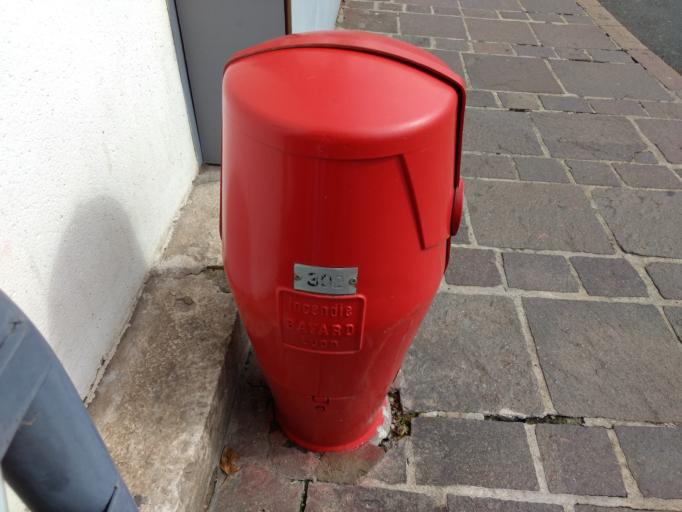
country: FR
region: Midi-Pyrenees
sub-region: Departement de l'Aveyron
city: Rodez
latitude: 44.3496
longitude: 2.5762
